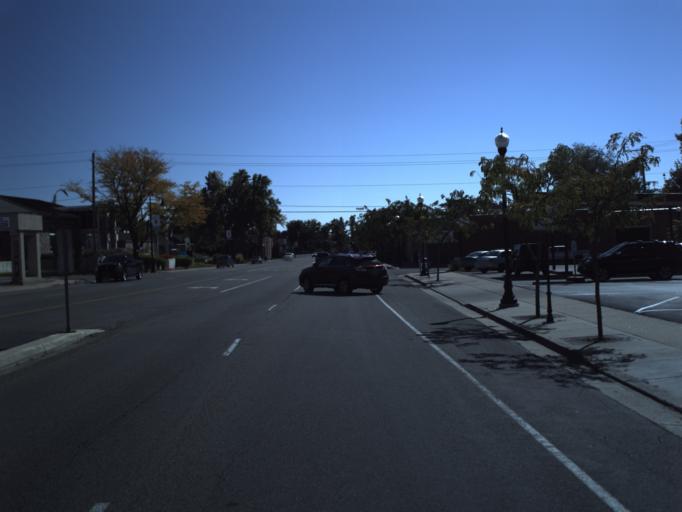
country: US
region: Utah
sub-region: Davis County
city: Kaysville
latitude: 41.0372
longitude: -111.9387
